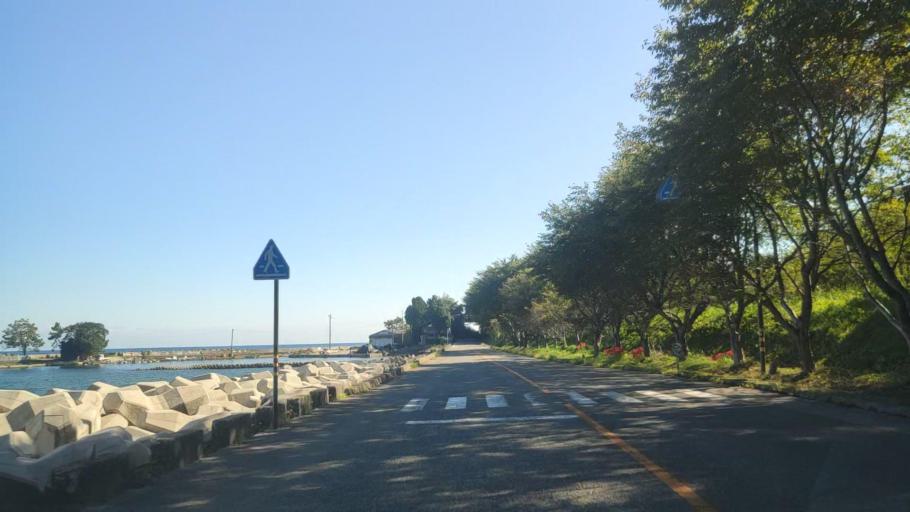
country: JP
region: Ishikawa
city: Nanao
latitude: 37.2756
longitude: 137.0967
